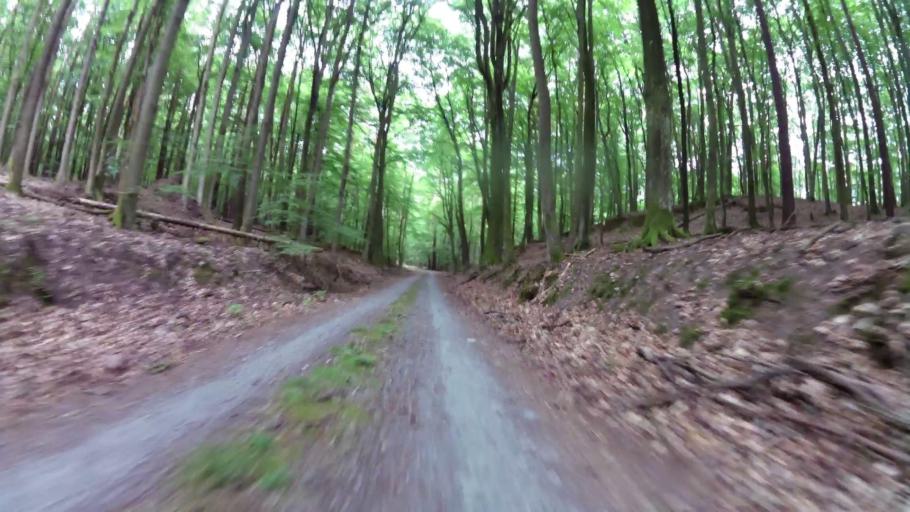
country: PL
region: West Pomeranian Voivodeship
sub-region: Powiat kamienski
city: Miedzyzdroje
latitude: 53.9475
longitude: 14.5546
